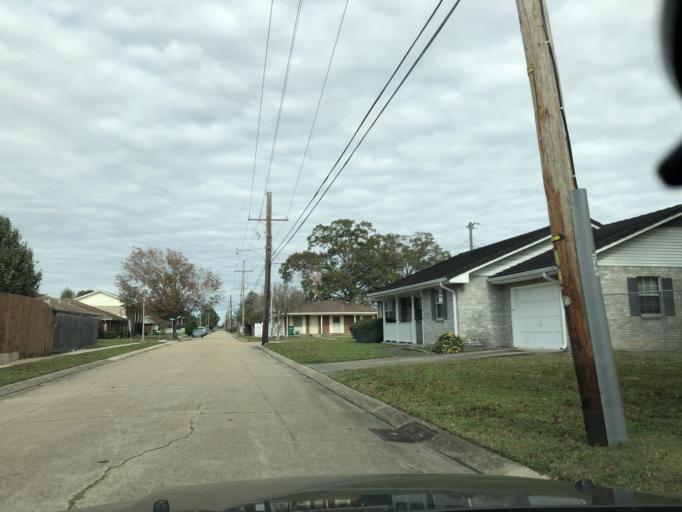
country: US
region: Louisiana
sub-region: Jefferson Parish
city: Metairie
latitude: 29.9873
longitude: -90.1613
